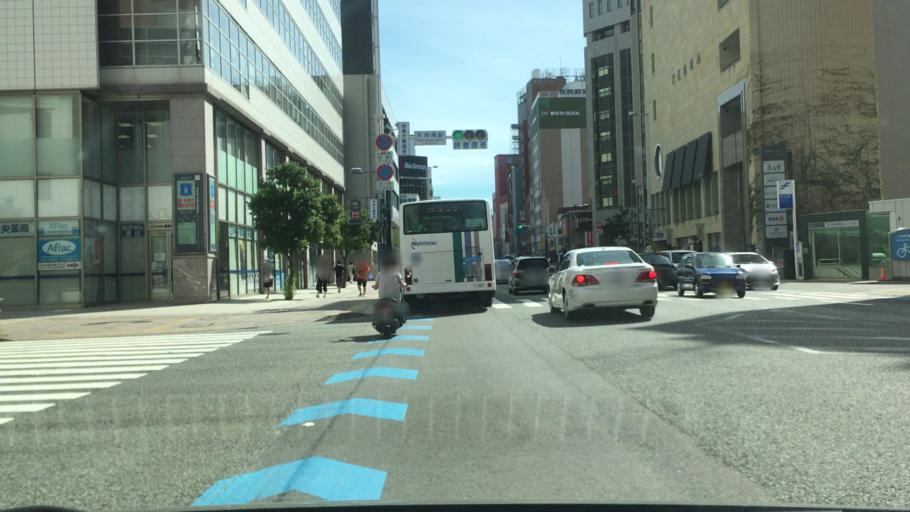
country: JP
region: Fukuoka
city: Fukuoka-shi
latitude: 33.5887
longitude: 130.4025
